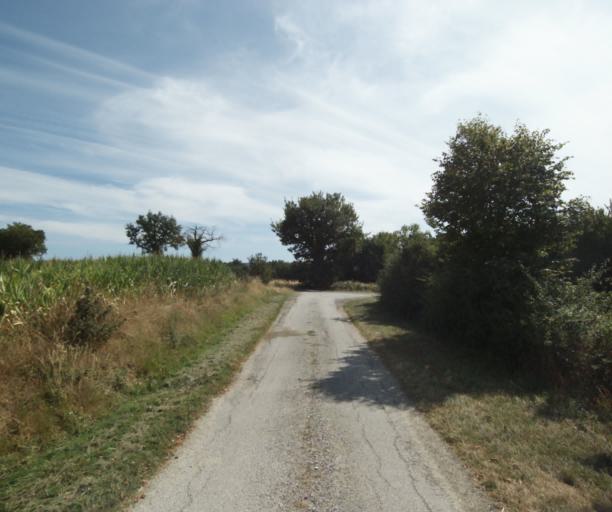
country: FR
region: Midi-Pyrenees
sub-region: Departement du Tarn
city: Soreze
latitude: 43.4972
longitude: 2.0503
